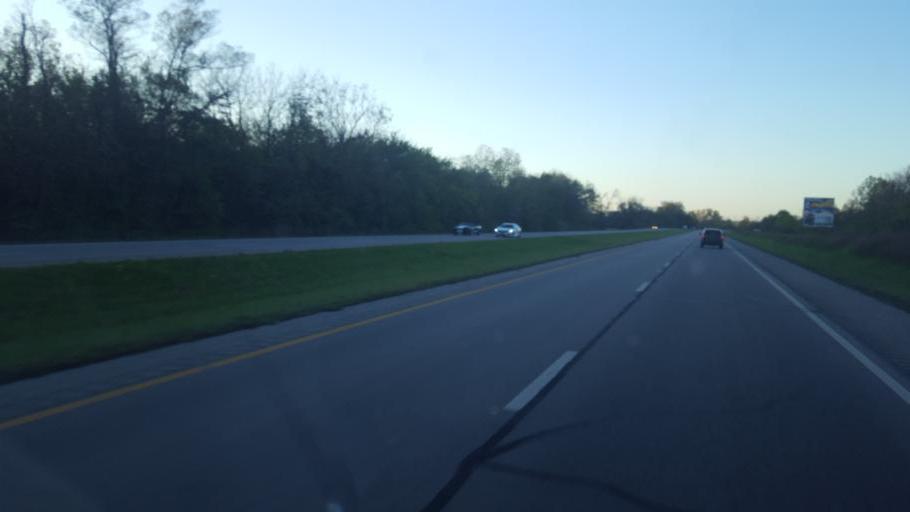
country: US
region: Ohio
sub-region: Pike County
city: Piketon
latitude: 38.9958
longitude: -83.0243
